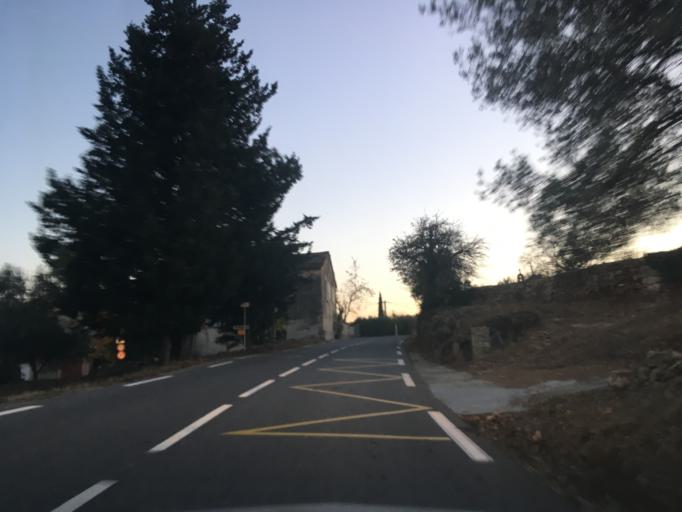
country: FR
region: Provence-Alpes-Cote d'Azur
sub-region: Departement du Var
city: Figanieres
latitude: 43.5471
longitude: 6.5292
